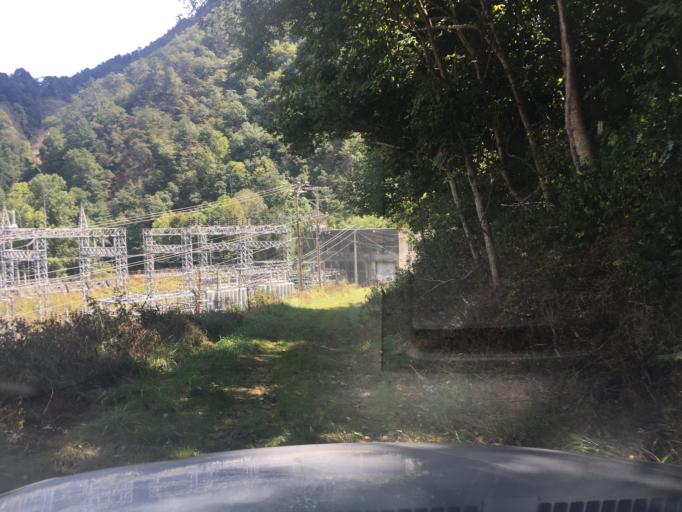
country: US
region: North Carolina
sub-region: Graham County
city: Robbinsville
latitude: 35.2713
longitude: -83.6775
